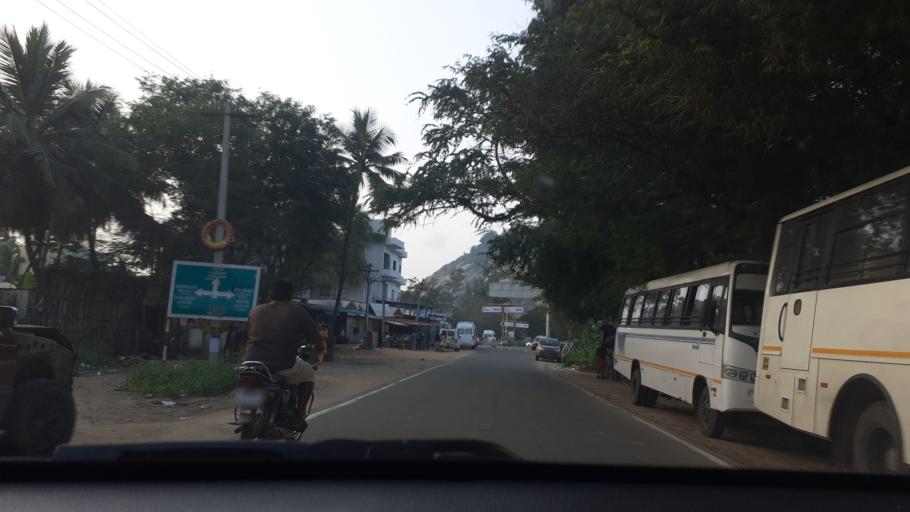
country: IN
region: Tamil Nadu
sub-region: Dindigul
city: Palani
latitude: 10.4317
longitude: 77.5241
